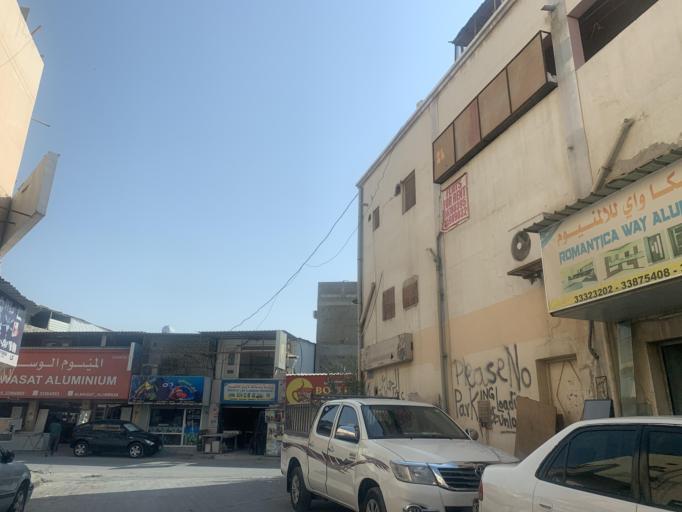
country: BH
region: Central Governorate
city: Madinat Hamad
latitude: 26.1419
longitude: 50.4921
